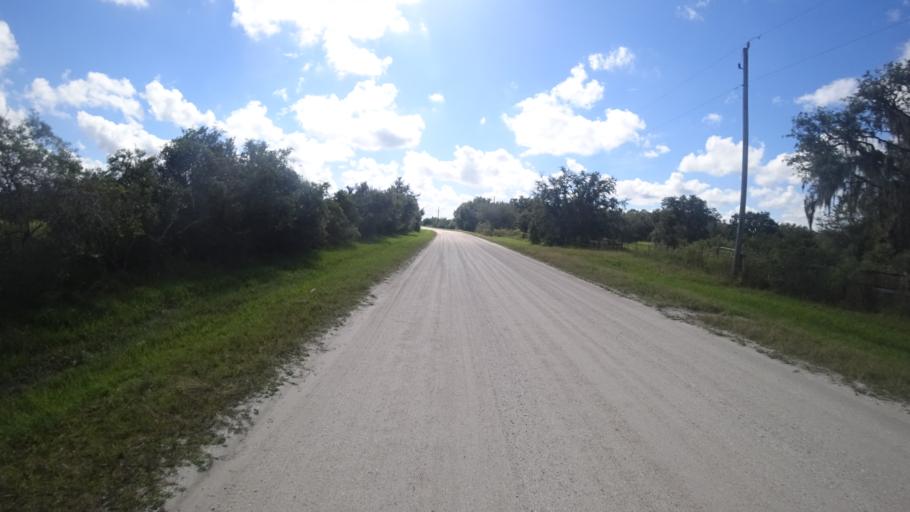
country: US
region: Florida
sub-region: DeSoto County
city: Arcadia
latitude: 27.3618
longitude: -82.1335
